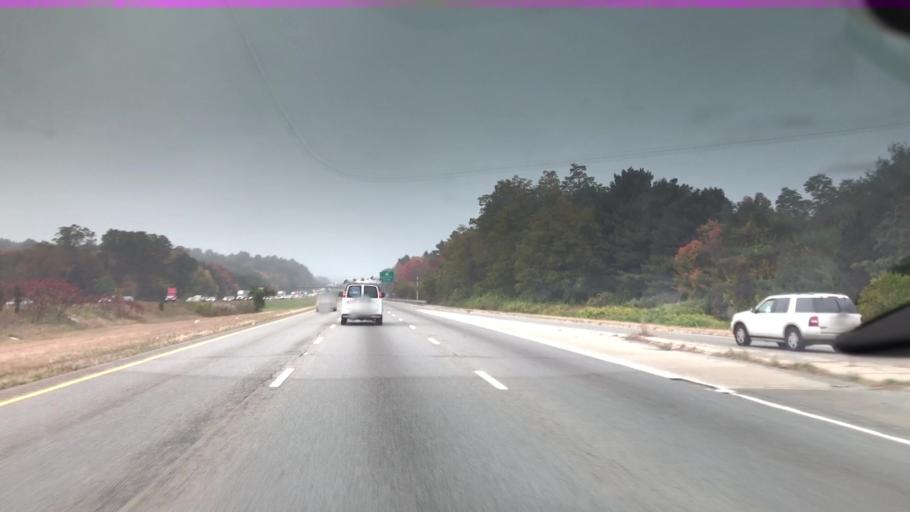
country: US
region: Massachusetts
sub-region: Middlesex County
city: Littleton Common
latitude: 42.5371
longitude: -71.4953
